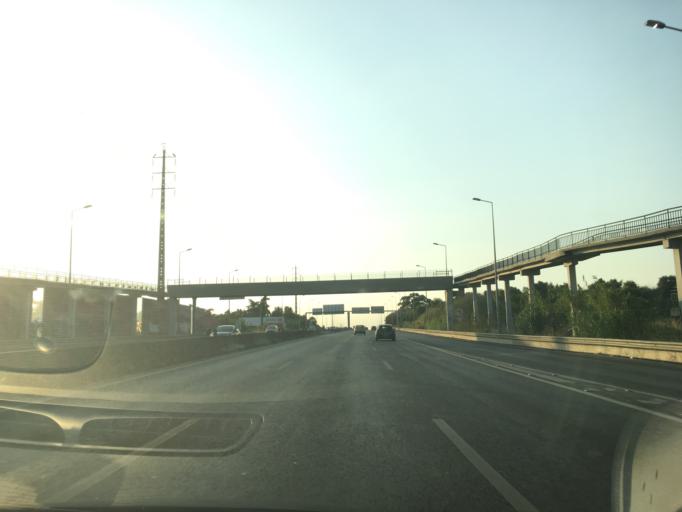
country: PT
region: Lisbon
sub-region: Sintra
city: Rio de Mouro
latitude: 38.7696
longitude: -9.3170
